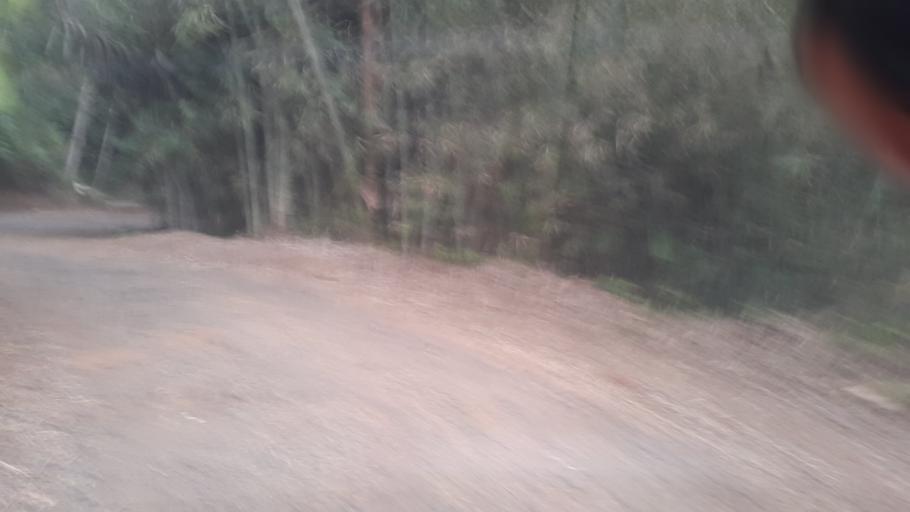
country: ID
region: West Java
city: Cigawir
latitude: -7.0824
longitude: 106.8932
